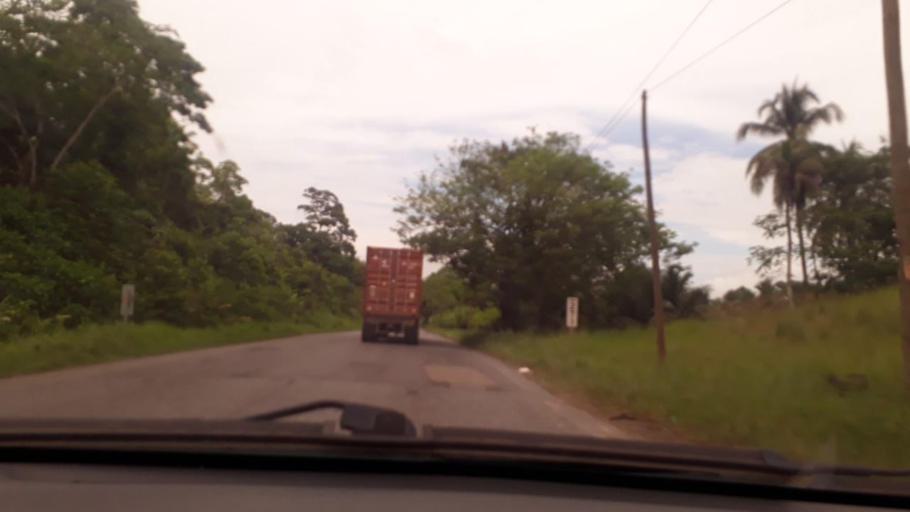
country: GT
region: Izabal
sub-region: Municipio de Puerto Barrios
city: Puerto Barrios
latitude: 15.5781
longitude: -88.6137
